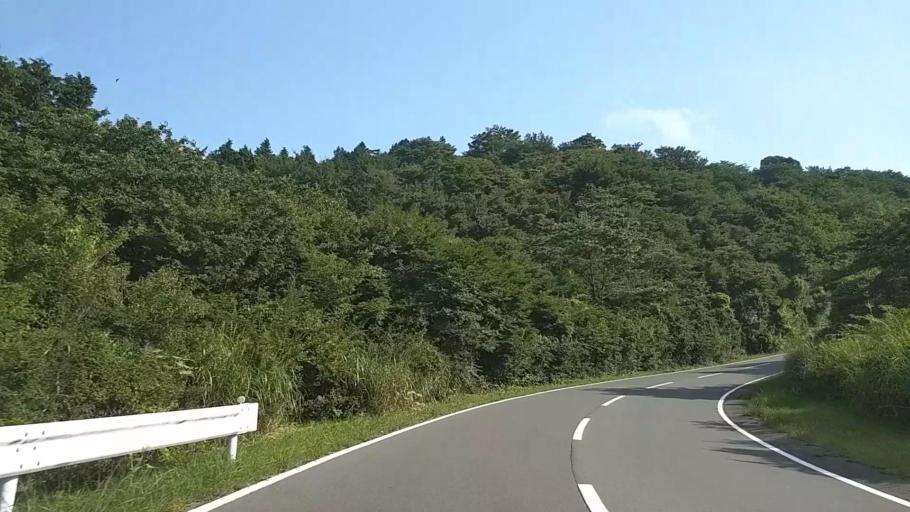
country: JP
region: Kanagawa
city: Hakone
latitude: 35.2281
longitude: 138.9808
